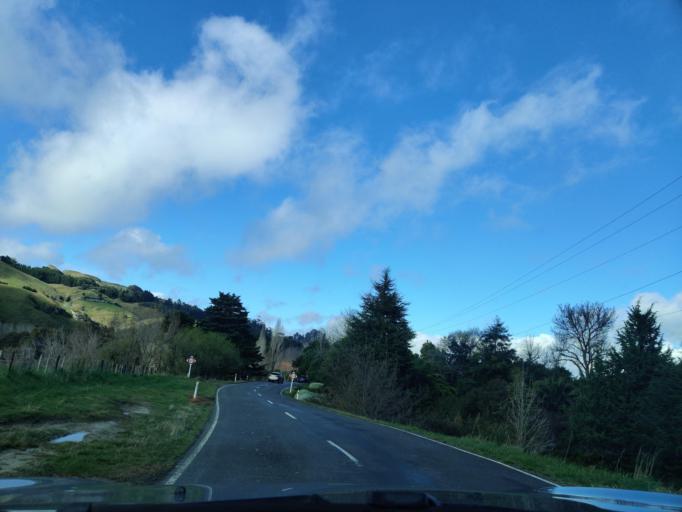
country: NZ
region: Hawke's Bay
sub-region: Hastings District
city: Hastings
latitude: -39.6843
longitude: 176.8984
